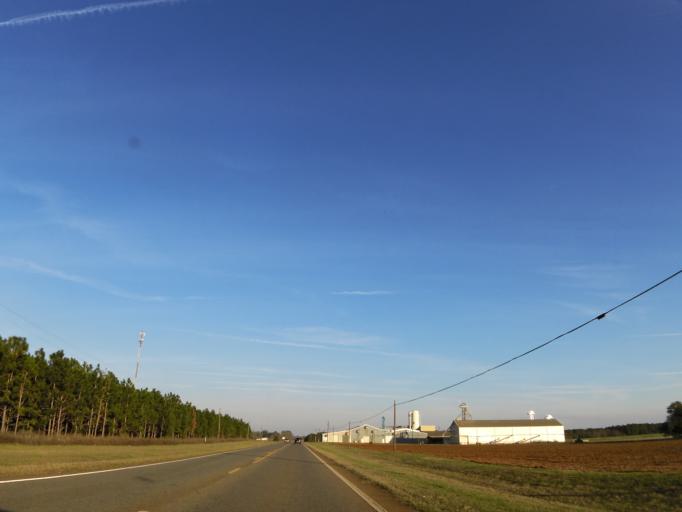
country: US
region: Georgia
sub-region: Sumter County
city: Americus
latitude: 32.0478
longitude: -84.3690
